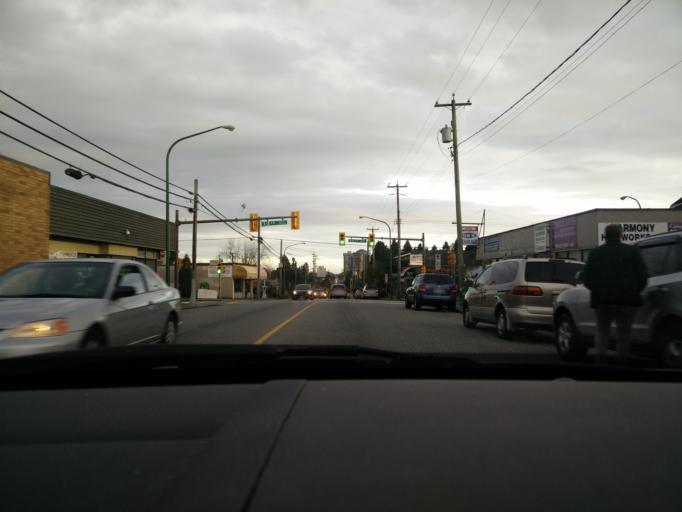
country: CA
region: British Columbia
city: New Westminster
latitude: 49.2222
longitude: -122.9318
